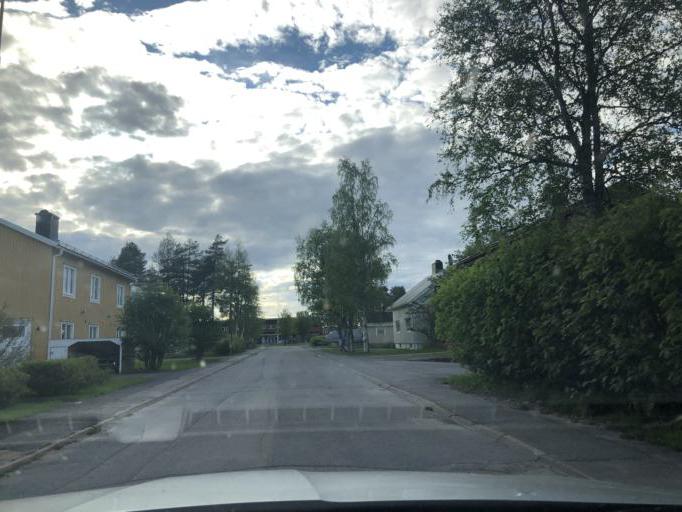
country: SE
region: Norrbotten
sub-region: Arvidsjaurs Kommun
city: Arvidsjaur
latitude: 65.5912
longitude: 19.1838
